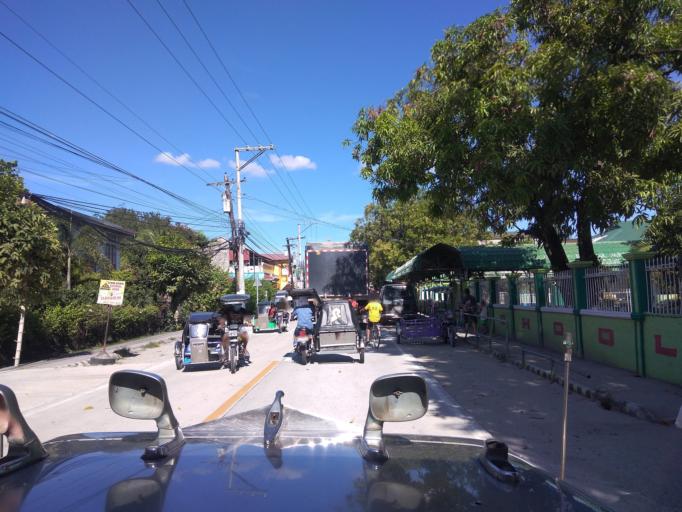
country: PH
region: Central Luzon
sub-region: Province of Pampanga
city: Santa Rita
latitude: 14.9966
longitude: 120.6159
